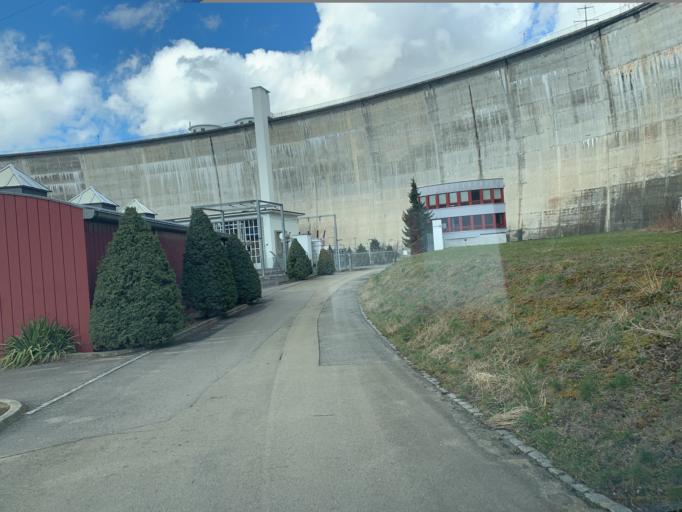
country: CH
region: Fribourg
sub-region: Sense District
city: Dudingen
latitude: 46.8822
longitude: 7.1954
